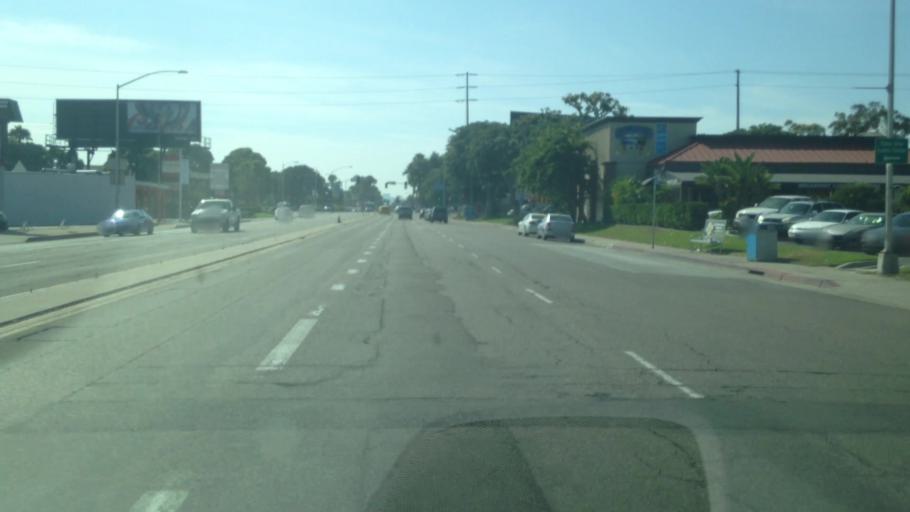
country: US
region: California
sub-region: San Diego County
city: San Diego
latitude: 32.7559
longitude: -117.2214
